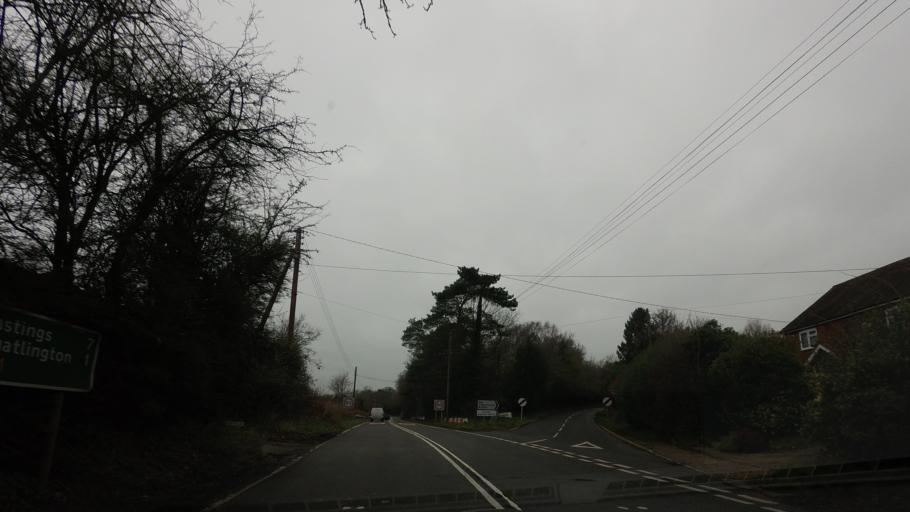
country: GB
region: England
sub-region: East Sussex
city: Battle
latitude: 50.9511
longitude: 0.5048
